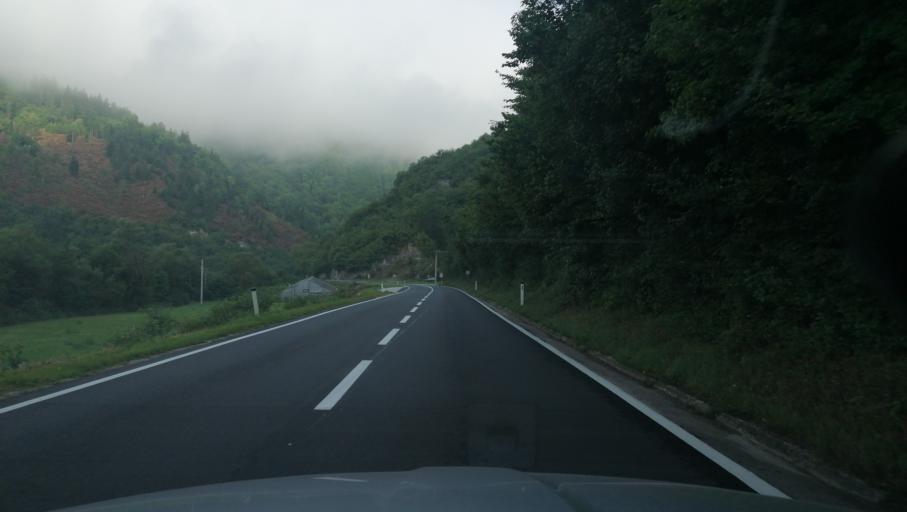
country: BA
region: Federation of Bosnia and Herzegovina
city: Donji Vakuf
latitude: 44.1845
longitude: 17.3480
